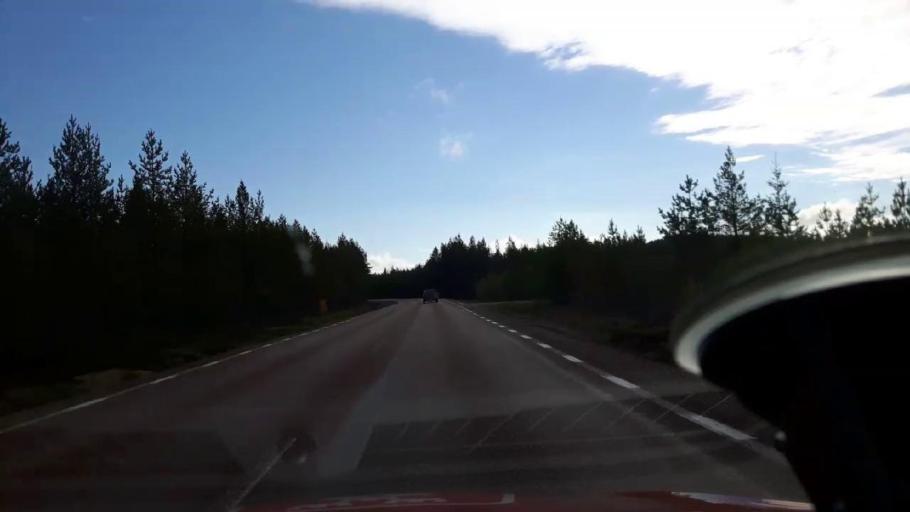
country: SE
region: Gaevleborg
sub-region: Ljusdals Kommun
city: Farila
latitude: 61.9393
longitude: 15.4857
